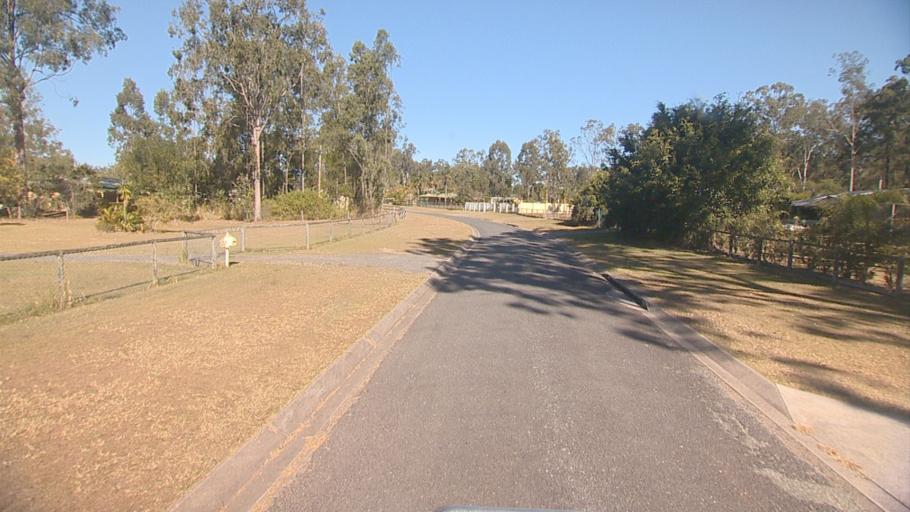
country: AU
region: Queensland
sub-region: Logan
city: North Maclean
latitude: -27.8164
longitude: 152.9467
